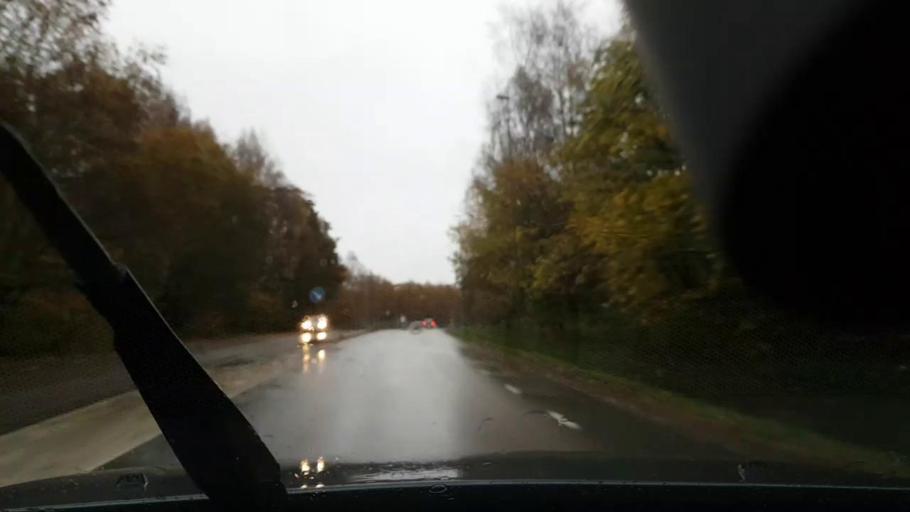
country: SE
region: Vaestra Goetaland
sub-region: Molndal
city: Kallered
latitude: 57.6024
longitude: 12.0598
